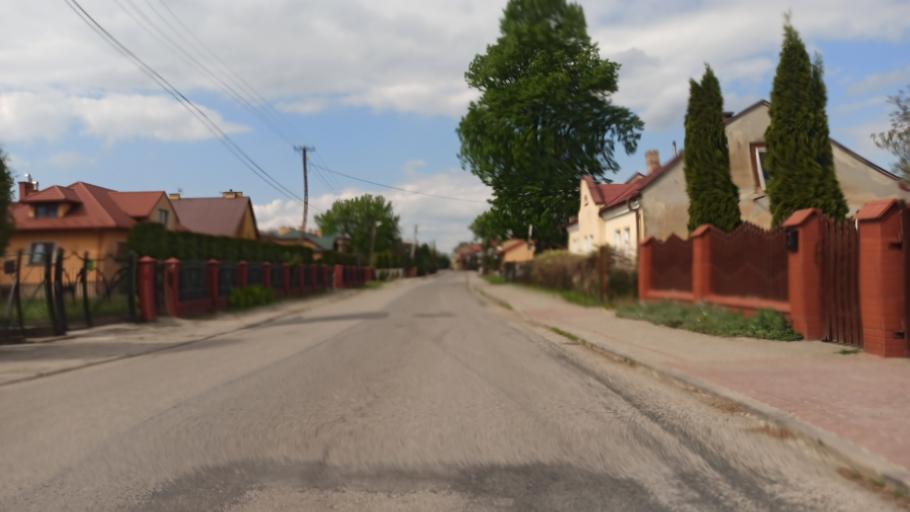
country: PL
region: Subcarpathian Voivodeship
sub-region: Powiat jaroslawski
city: Radymno
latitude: 49.9490
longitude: 22.8150
